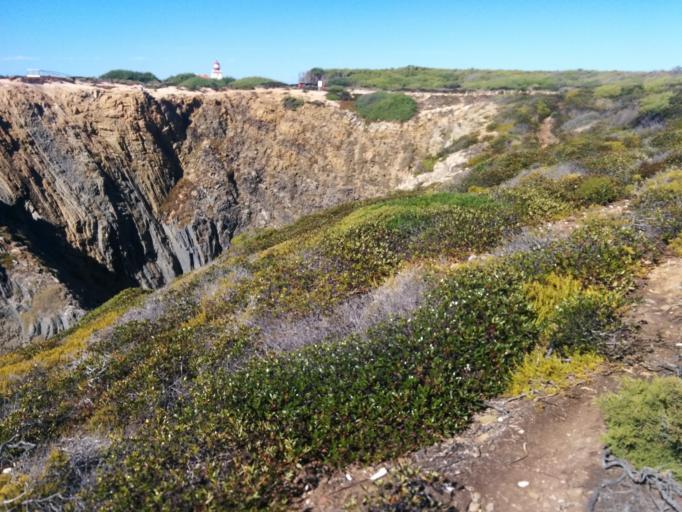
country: PT
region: Beja
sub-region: Odemira
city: Vila Nova de Milfontes
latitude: 37.5954
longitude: -8.8171
